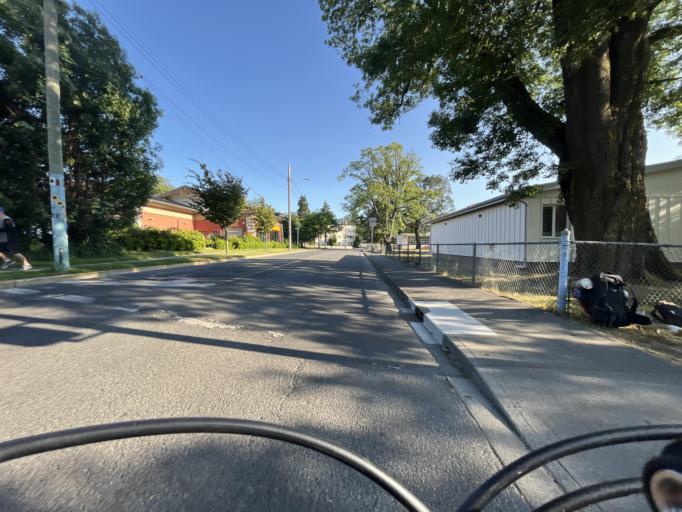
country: CA
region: British Columbia
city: Victoria
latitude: 48.4244
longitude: -123.3456
